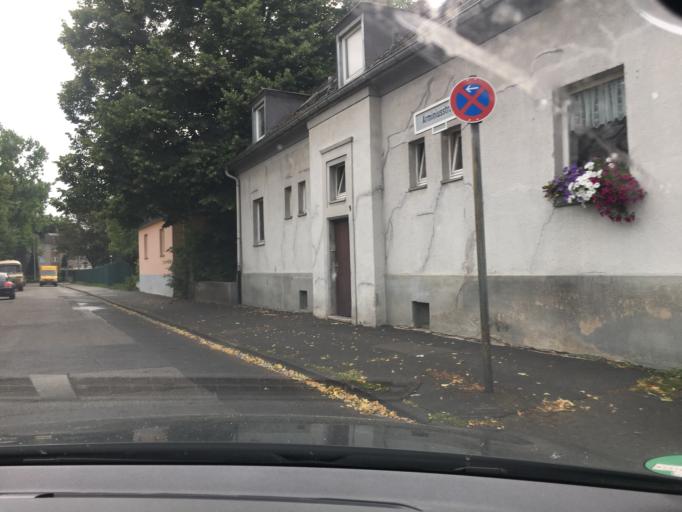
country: DE
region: North Rhine-Westphalia
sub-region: Regierungsbezirk Koln
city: Bonn
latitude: 50.7515
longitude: 7.0953
